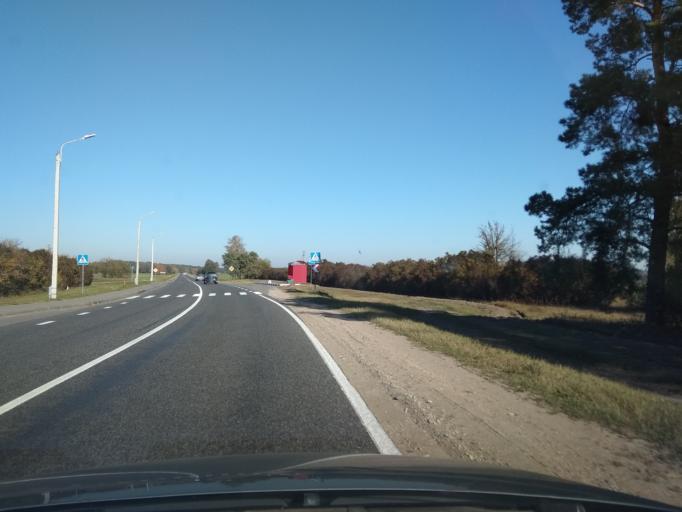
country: BY
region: Brest
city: Kobryn
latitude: 52.1185
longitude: 24.3053
